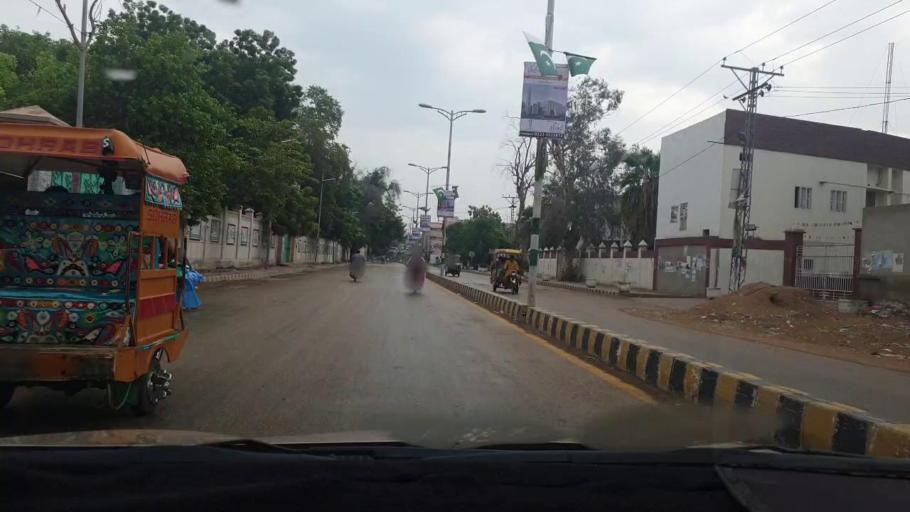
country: PK
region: Sindh
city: Larkana
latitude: 27.5545
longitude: 68.2078
